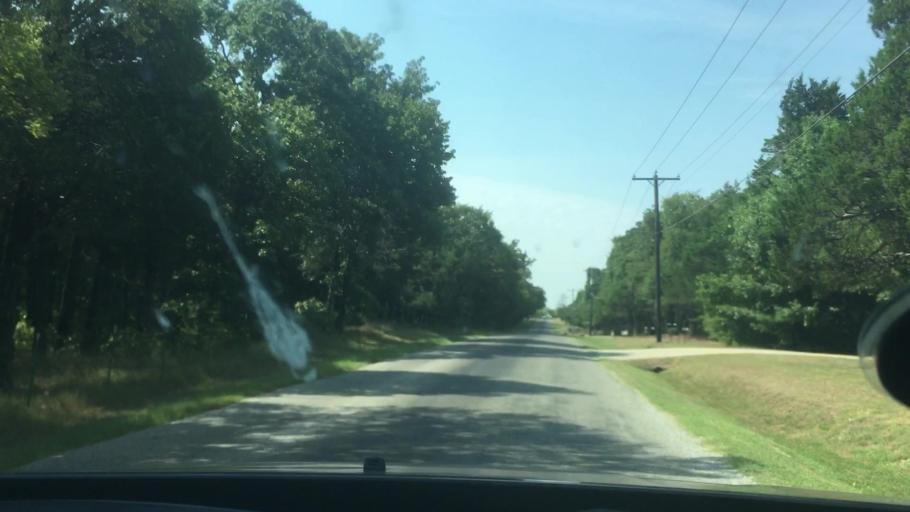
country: US
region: Texas
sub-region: Grayson County
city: Pottsboro
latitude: 33.8135
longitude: -96.7030
